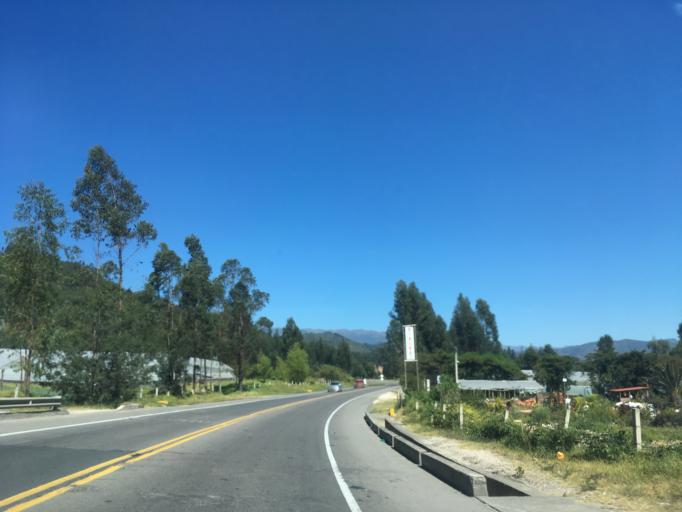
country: CO
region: Boyaca
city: Tibasosa
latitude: 5.7582
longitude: -72.9955
